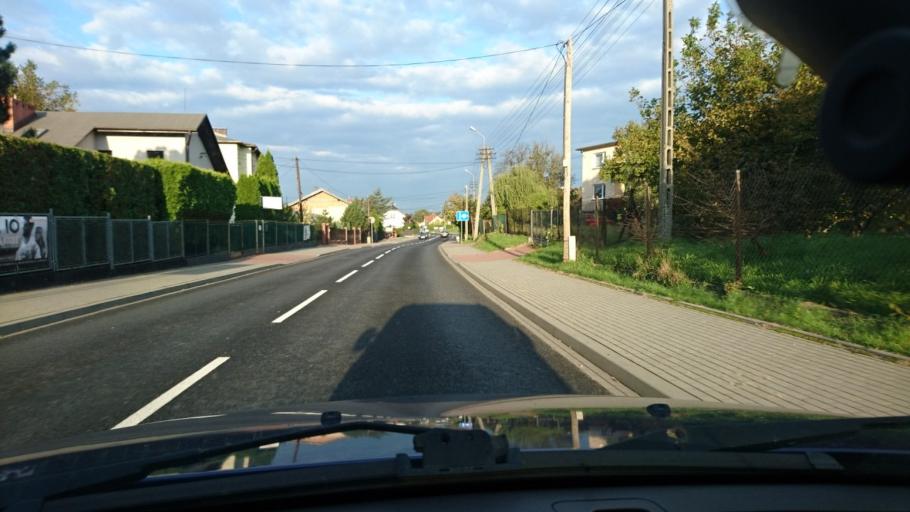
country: PL
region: Silesian Voivodeship
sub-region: Bielsko-Biala
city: Bielsko-Biala
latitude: 49.8403
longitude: 19.0641
